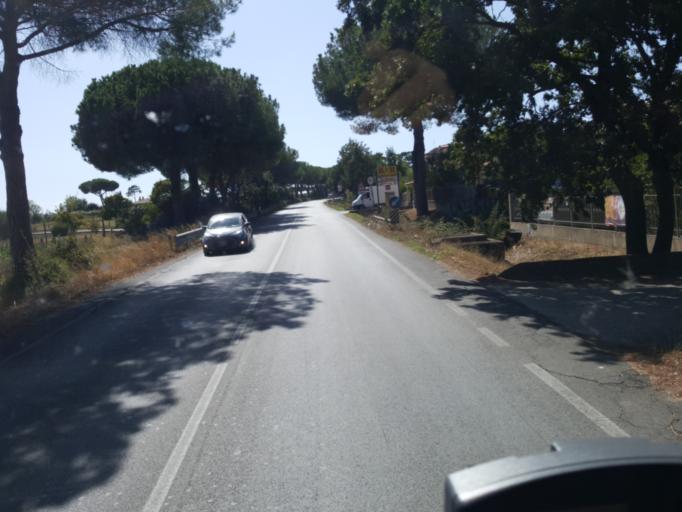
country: IT
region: Latium
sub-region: Provincia di Latina
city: Genio Civile
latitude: 41.5388
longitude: 12.7208
